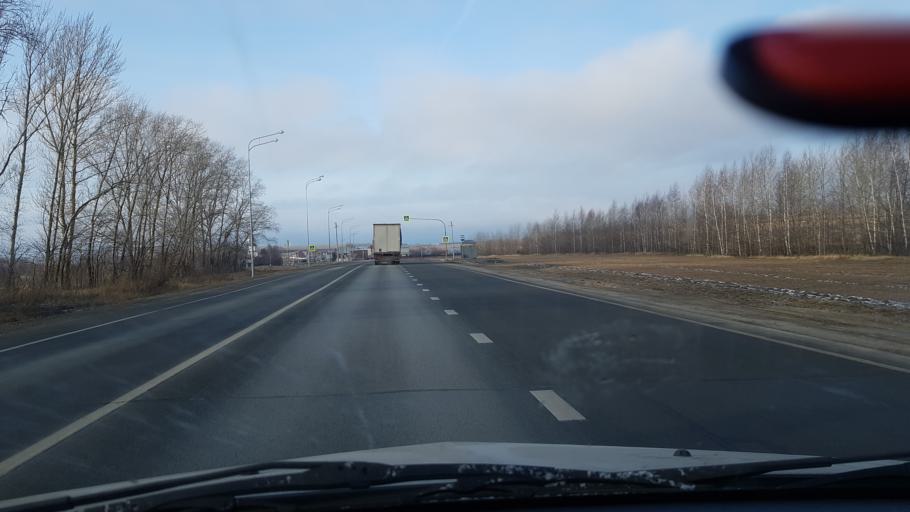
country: RU
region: Tatarstan
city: Laishevo
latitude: 55.3910
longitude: 49.8100
